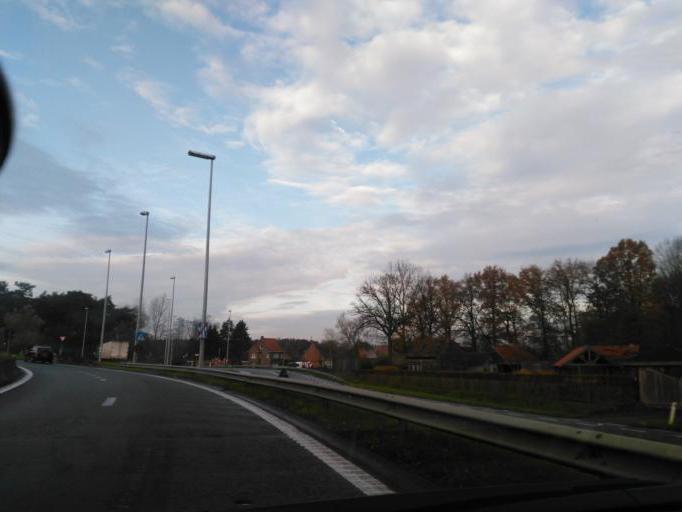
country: BE
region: Flanders
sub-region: Provincie Oost-Vlaanderen
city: Stekene
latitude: 51.2292
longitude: 4.0627
